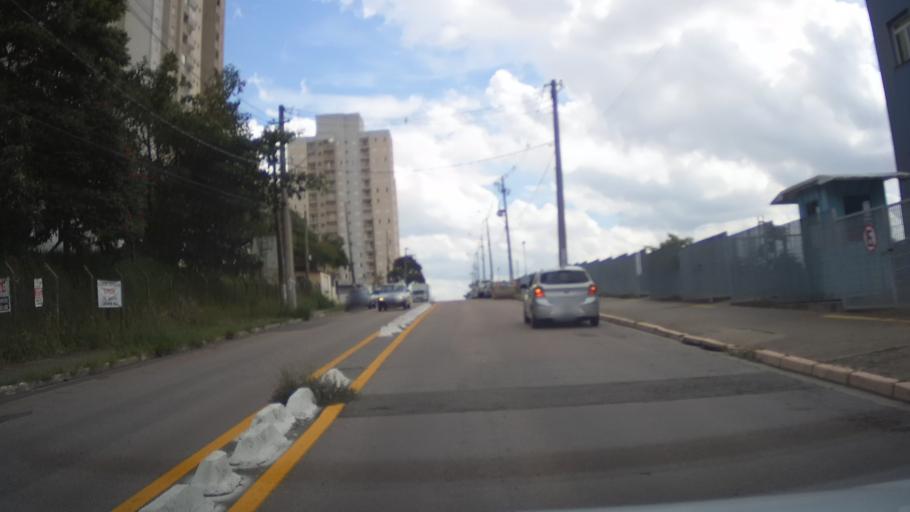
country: BR
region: Sao Paulo
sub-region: Campinas
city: Campinas
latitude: -22.9257
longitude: -47.0361
